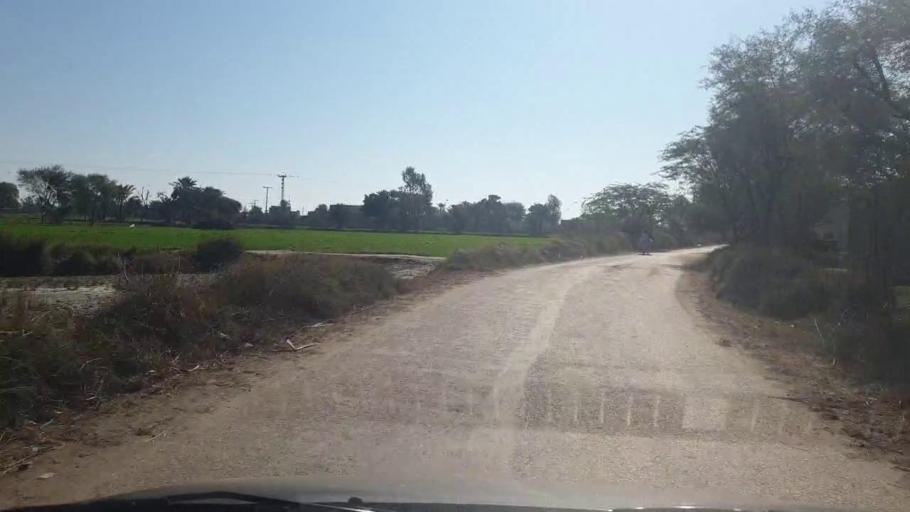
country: PK
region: Sindh
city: Bozdar
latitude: 27.1548
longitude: 68.6544
